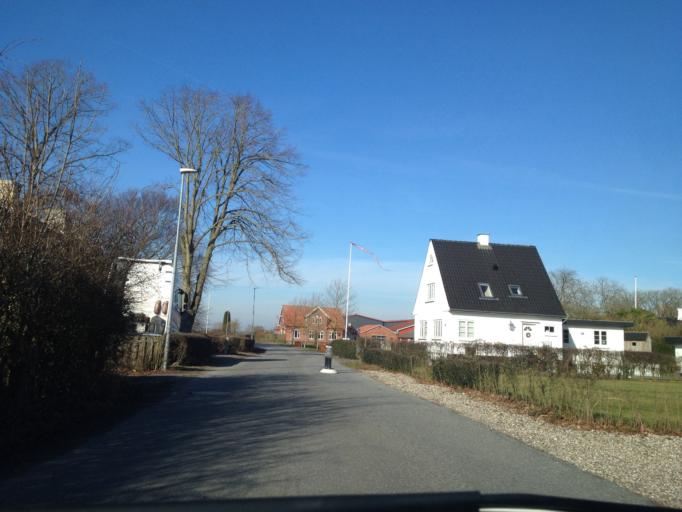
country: DK
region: South Denmark
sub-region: Nyborg Kommune
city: Ullerslev
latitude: 55.3883
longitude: 10.7062
